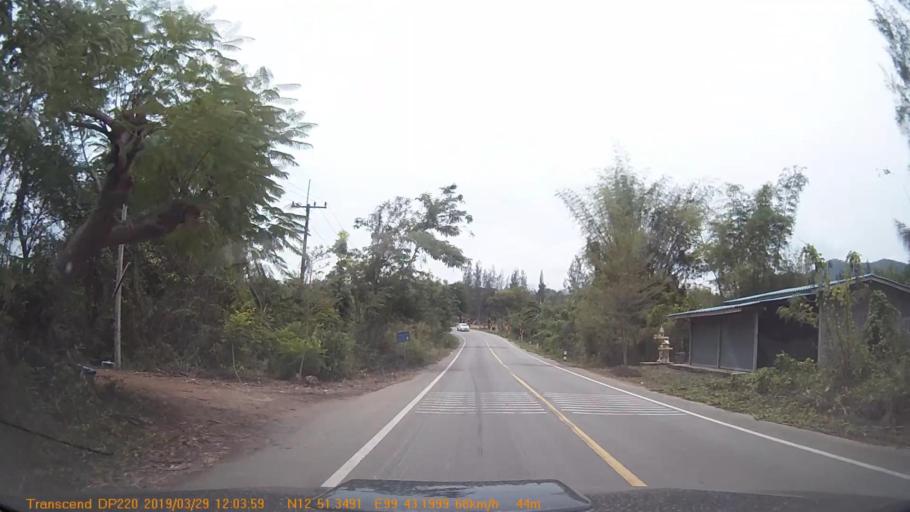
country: TH
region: Phetchaburi
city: Kaeng Krachan
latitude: 12.8554
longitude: 99.7201
